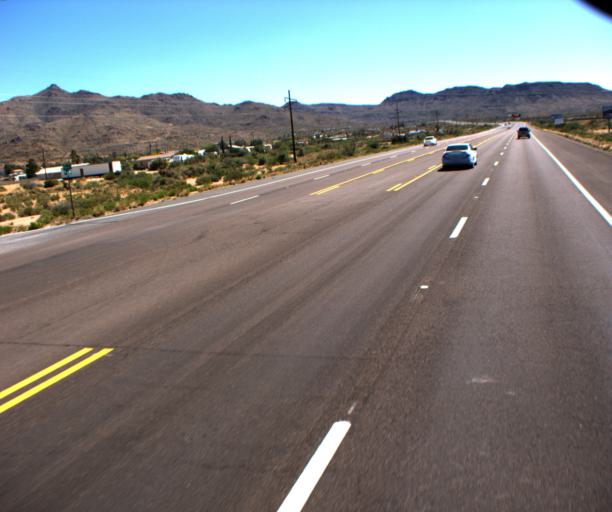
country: US
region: Arizona
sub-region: Mohave County
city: Golden Valley
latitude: 35.2187
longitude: -114.1501
